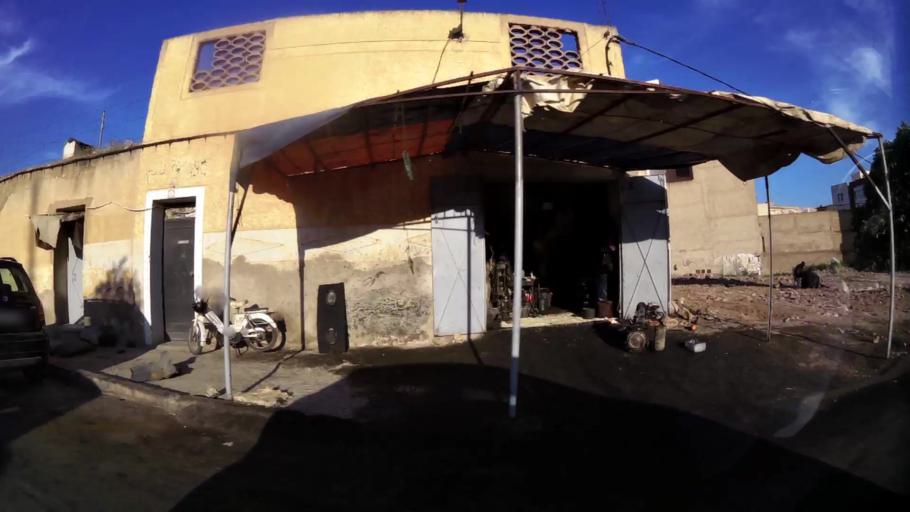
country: MA
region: Oriental
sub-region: Oujda-Angad
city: Oujda
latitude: 34.6954
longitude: -1.9050
